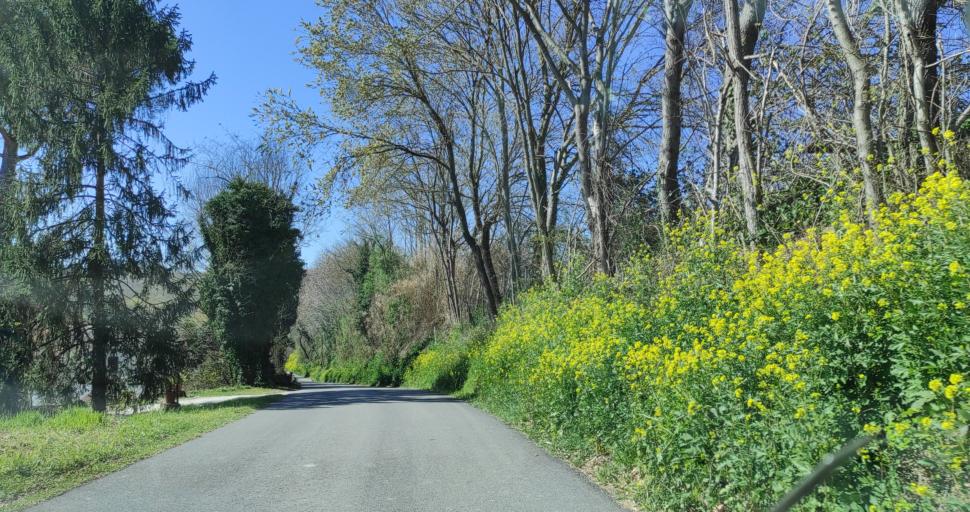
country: IT
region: The Marches
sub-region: Provincia di Macerata
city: Macerata
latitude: 43.3128
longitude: 13.4823
